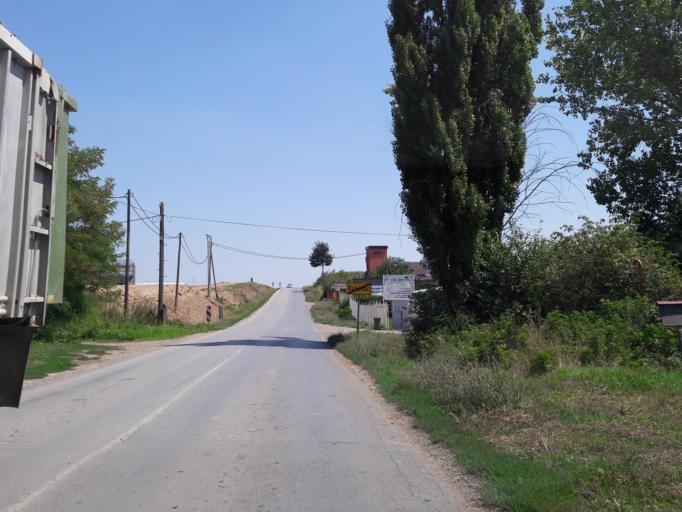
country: HR
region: Osjecko-Baranjska
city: Viskovci
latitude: 45.3457
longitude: 18.4266
